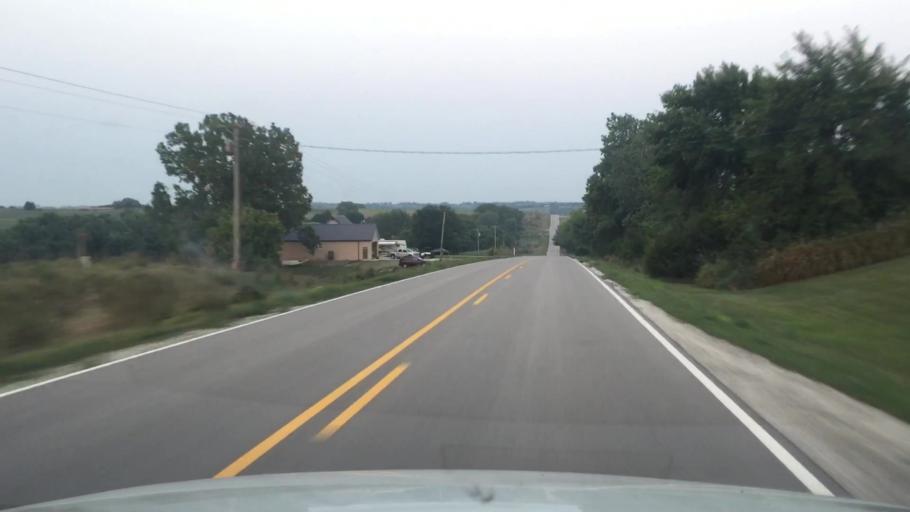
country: US
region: Iowa
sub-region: Warren County
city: Indianola
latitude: 41.1906
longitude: -93.5670
